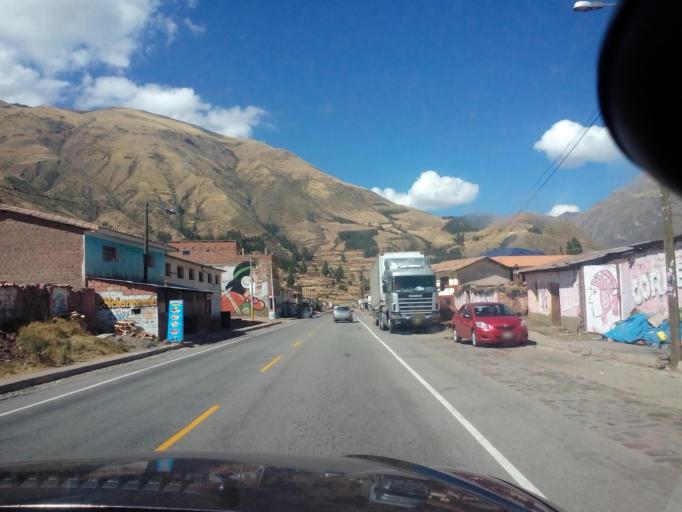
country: PE
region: Cusco
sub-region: Provincia de Quispicanchis
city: Cusipata
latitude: -13.9033
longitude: -71.4999
